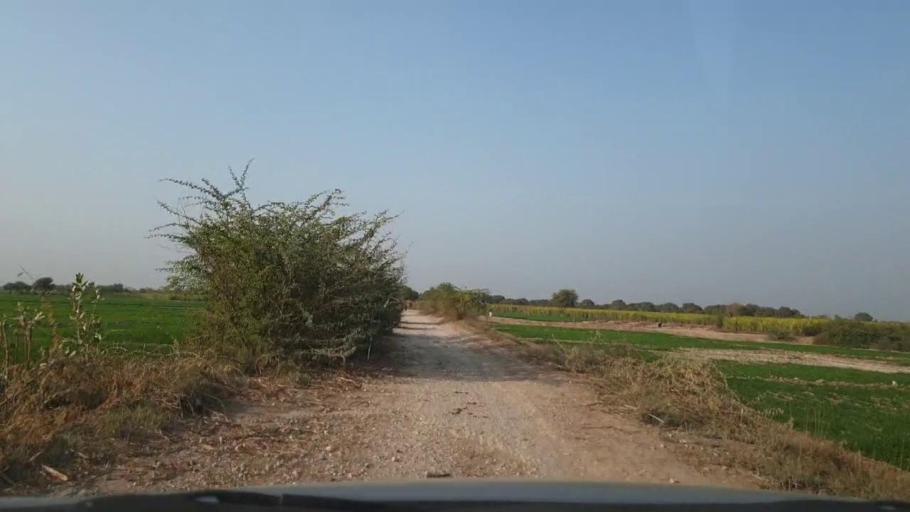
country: PK
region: Sindh
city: Tando Adam
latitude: 25.6743
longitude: 68.6366
